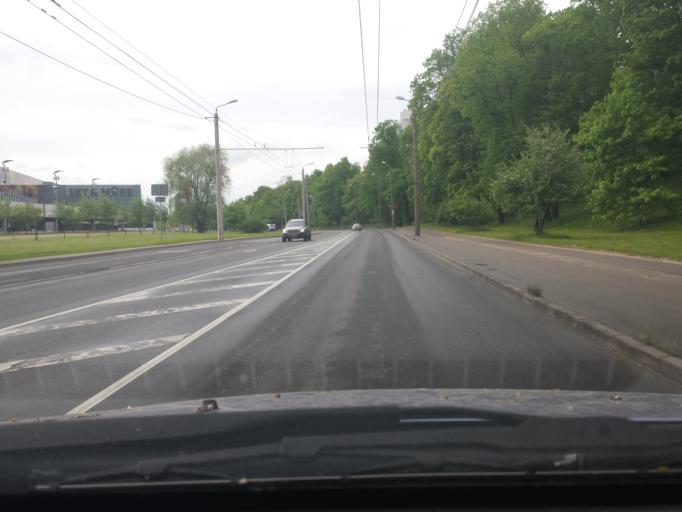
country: LV
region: Riga
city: Riga
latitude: 56.9851
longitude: 24.1351
